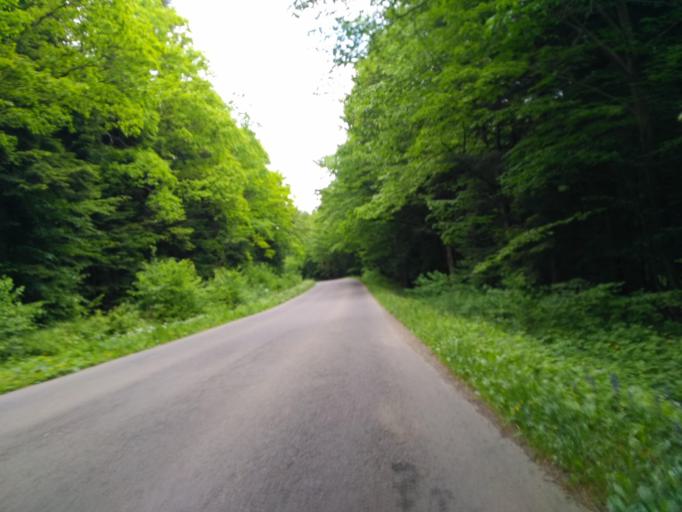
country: PL
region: Subcarpathian Voivodeship
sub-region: Powiat krosnienski
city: Chorkowka
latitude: 49.6310
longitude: 21.6556
